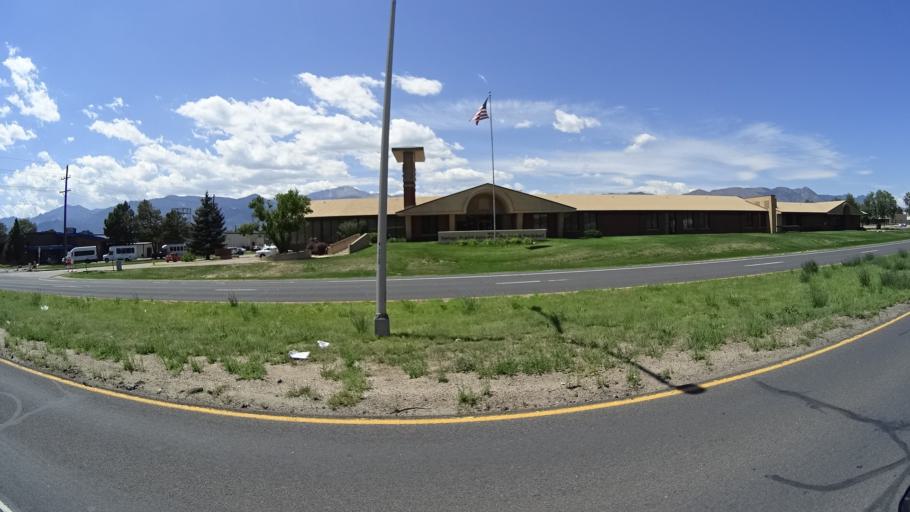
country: US
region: Colorado
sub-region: El Paso County
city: Colorado Springs
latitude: 38.8819
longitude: -104.8186
